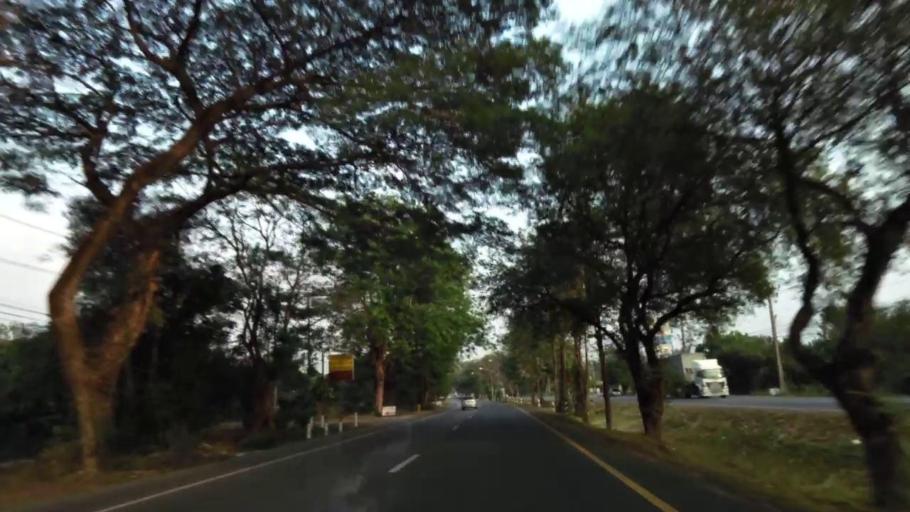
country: TH
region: Chanthaburi
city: Khlung
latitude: 12.4652
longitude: 102.2122
